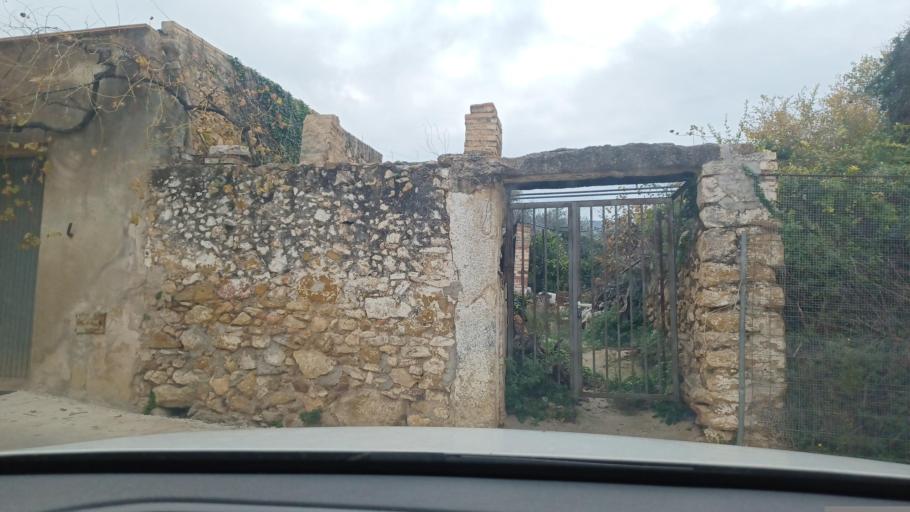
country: ES
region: Catalonia
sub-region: Provincia de Tarragona
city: Santa Barbara
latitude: 40.6559
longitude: 0.4713
